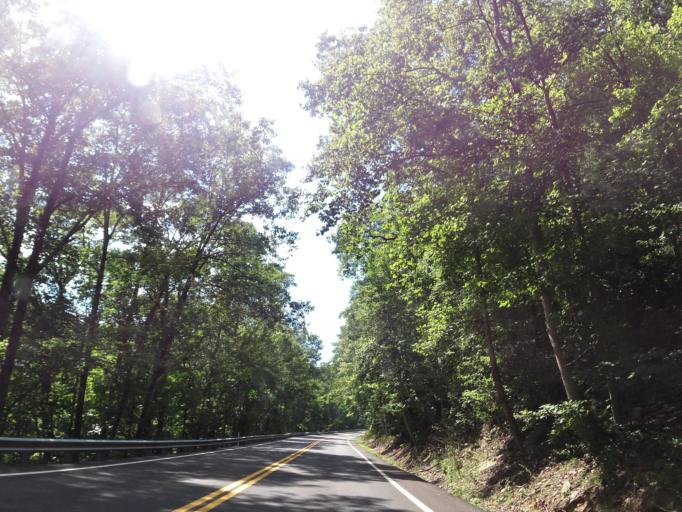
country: US
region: Tennessee
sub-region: Roane County
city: Rockwood
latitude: 35.8785
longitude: -84.8164
